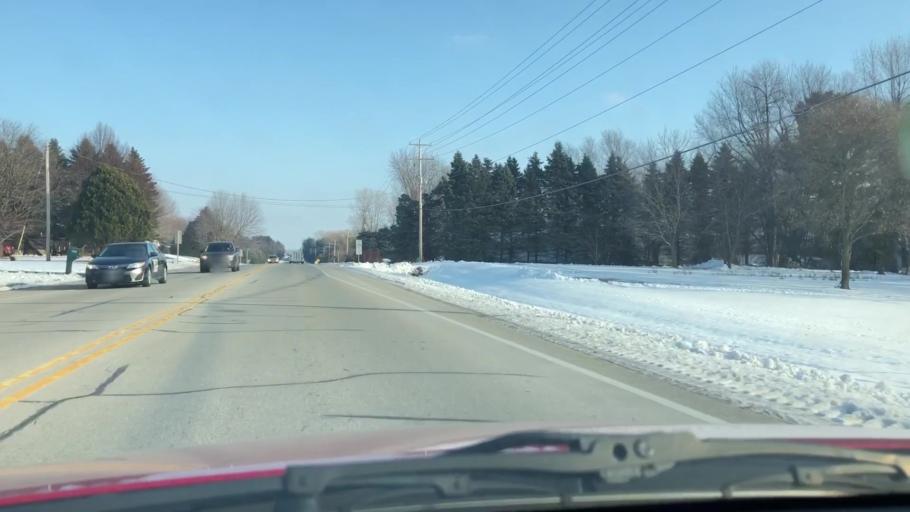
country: US
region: Wisconsin
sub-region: Outagamie County
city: Appleton
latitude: 44.3164
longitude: -88.3902
